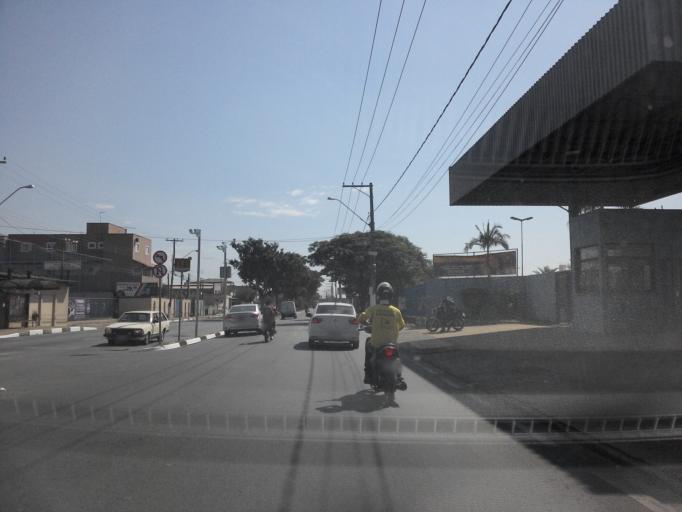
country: BR
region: Sao Paulo
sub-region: Hortolandia
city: Hortolandia
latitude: -22.8936
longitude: -47.2303
